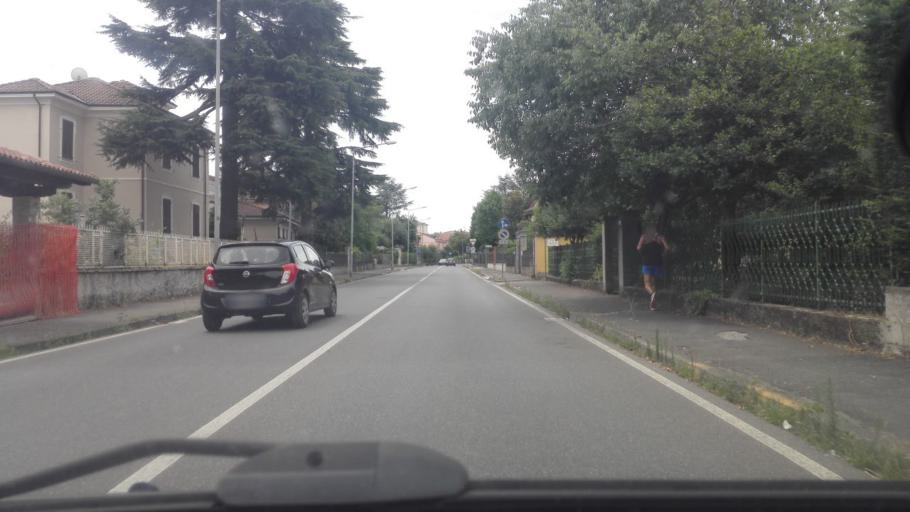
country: IT
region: Piedmont
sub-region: Provincia di Alessandria
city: Novi Ligure
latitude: 44.7672
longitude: 8.7979
